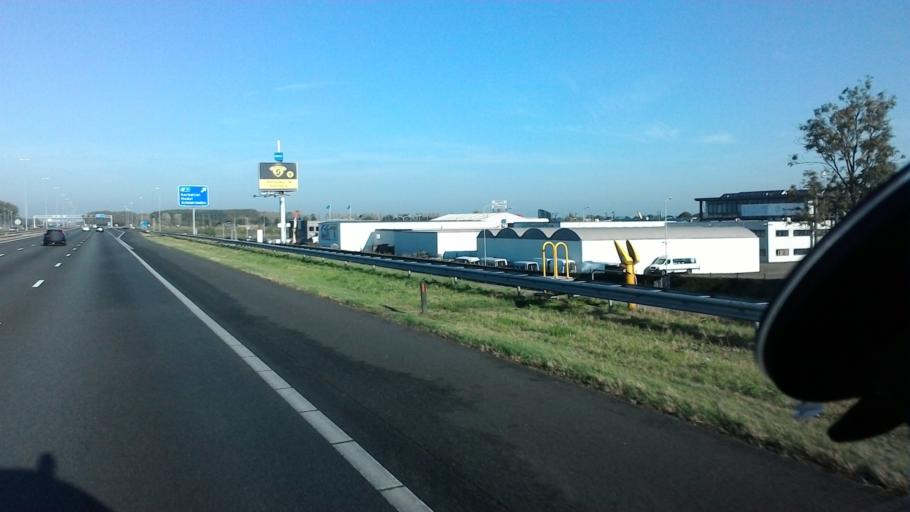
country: NL
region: Gelderland
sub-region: Gemeente Maasdriel
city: Hedel
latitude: 51.7545
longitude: 5.2873
